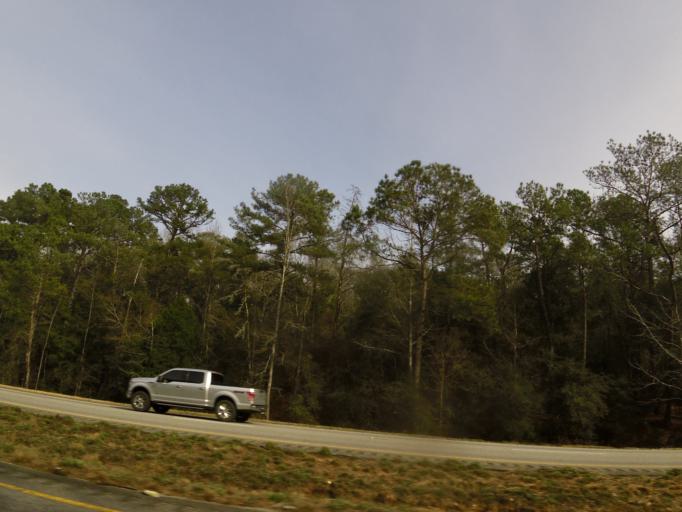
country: US
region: Alabama
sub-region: Dale County
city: Newton
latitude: 31.3514
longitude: -85.5556
